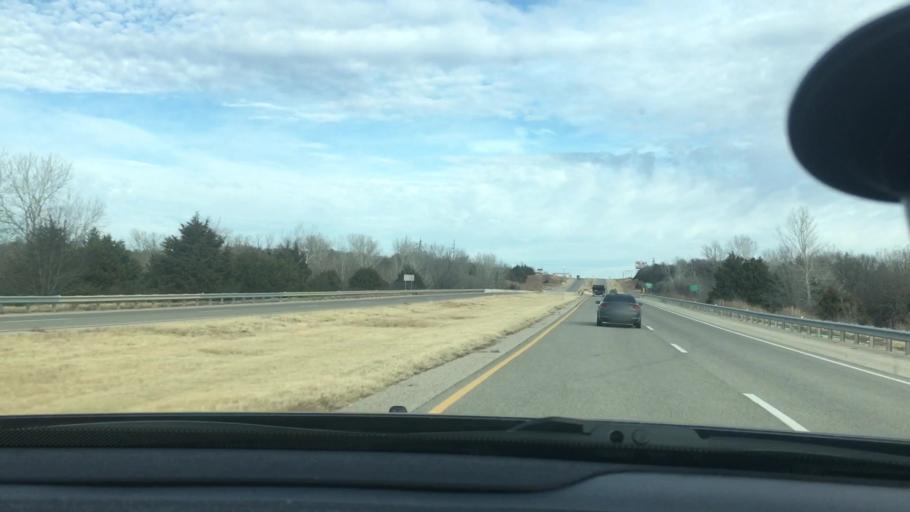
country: US
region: Oklahoma
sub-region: Pontotoc County
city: Byng
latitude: 34.9295
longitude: -96.6837
